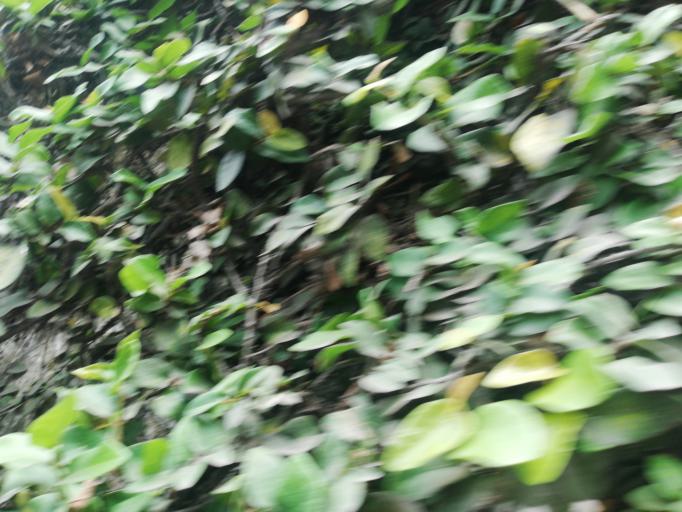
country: PH
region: Central Visayas
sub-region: Province of Negros Oriental
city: Dumaguete
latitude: 9.3047
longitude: 123.3006
